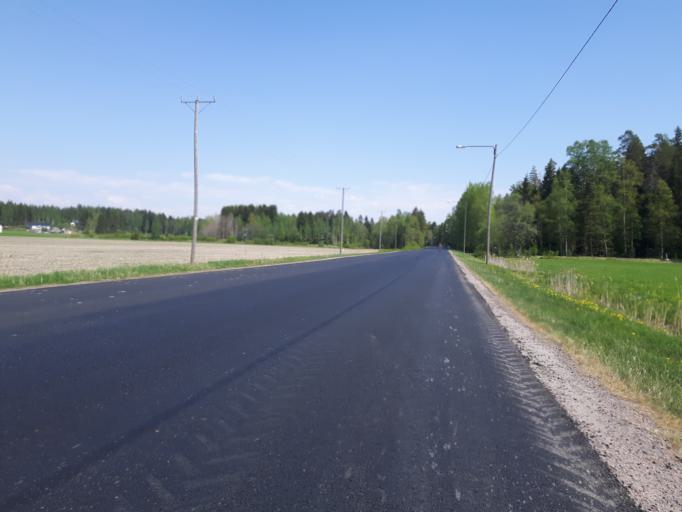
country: FI
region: Uusimaa
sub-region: Helsinki
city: Pornainen
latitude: 60.3336
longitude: 25.4545
